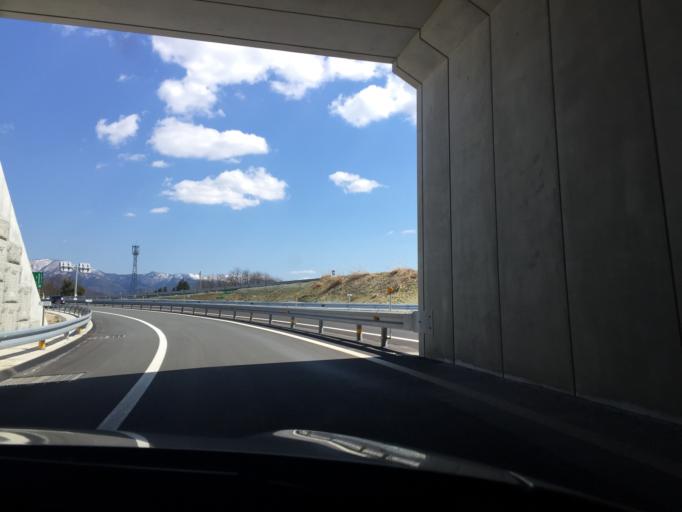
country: JP
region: Yamagata
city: Takahata
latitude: 38.0249
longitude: 140.1638
